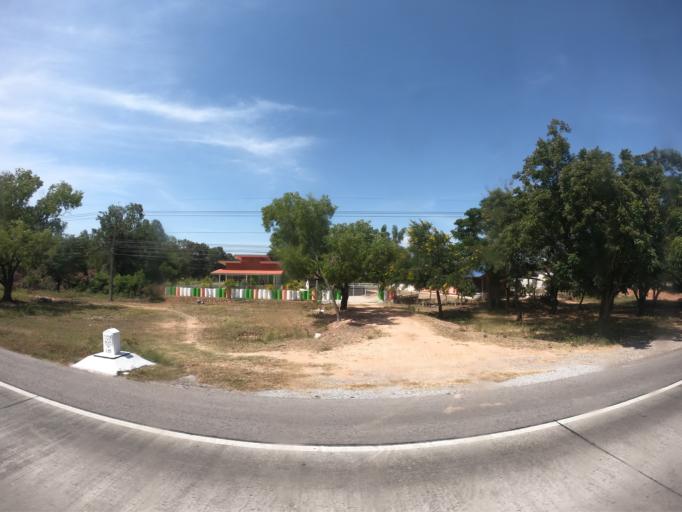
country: TH
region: Nakhon Ratchasima
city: Sida
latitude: 15.5654
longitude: 102.5524
